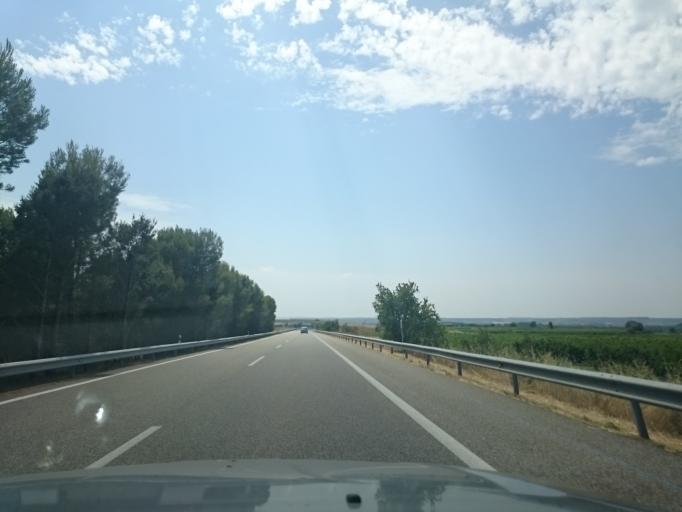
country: ES
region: Catalonia
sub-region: Provincia de Lleida
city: Torres de Segre
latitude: 41.5406
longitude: 0.5435
